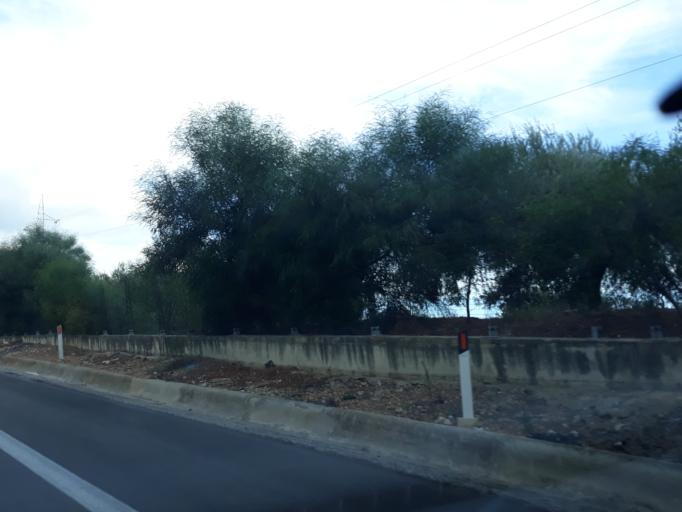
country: IT
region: Sicily
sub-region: Palermo
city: Termini Imerese
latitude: 37.9821
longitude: 13.6663
